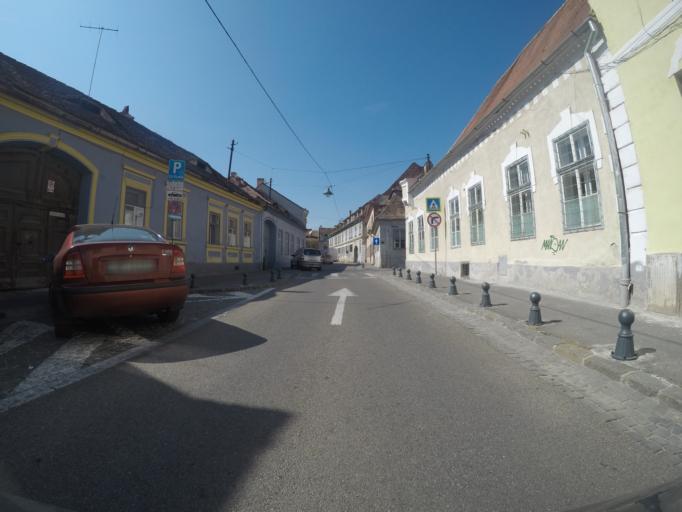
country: RO
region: Sibiu
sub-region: Municipiul Sibiu
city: Sibiu
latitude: 45.7965
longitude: 24.1548
